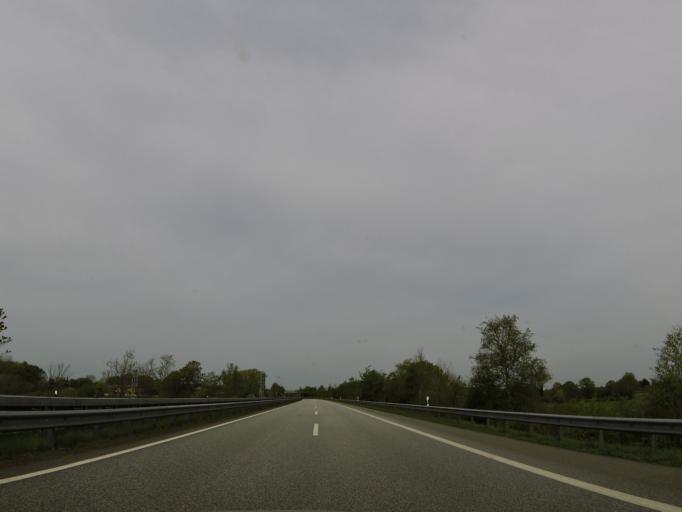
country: DE
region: Schleswig-Holstein
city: Kaisborstel
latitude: 54.0115
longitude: 9.4727
